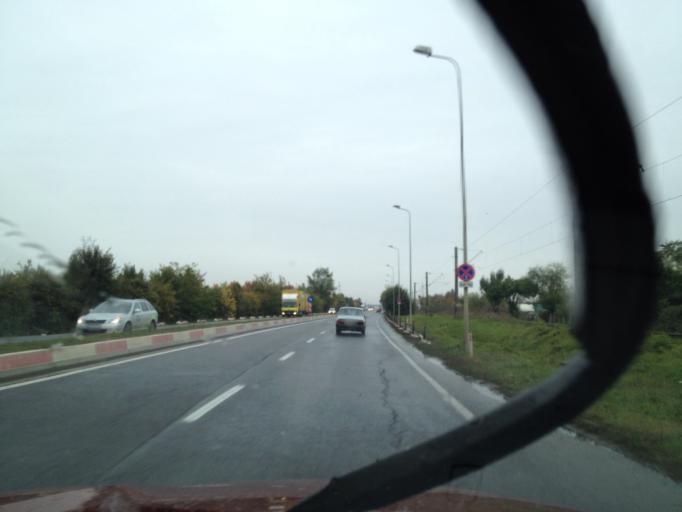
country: RO
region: Brasov
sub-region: Comuna Sanpetru
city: Sanpetru
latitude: 45.6758
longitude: 25.6487
